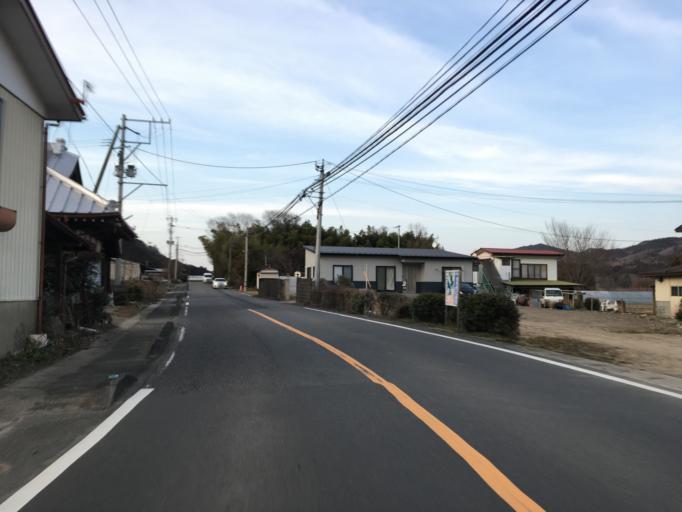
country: JP
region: Ibaraki
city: Daigo
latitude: 36.9109
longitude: 140.4083
